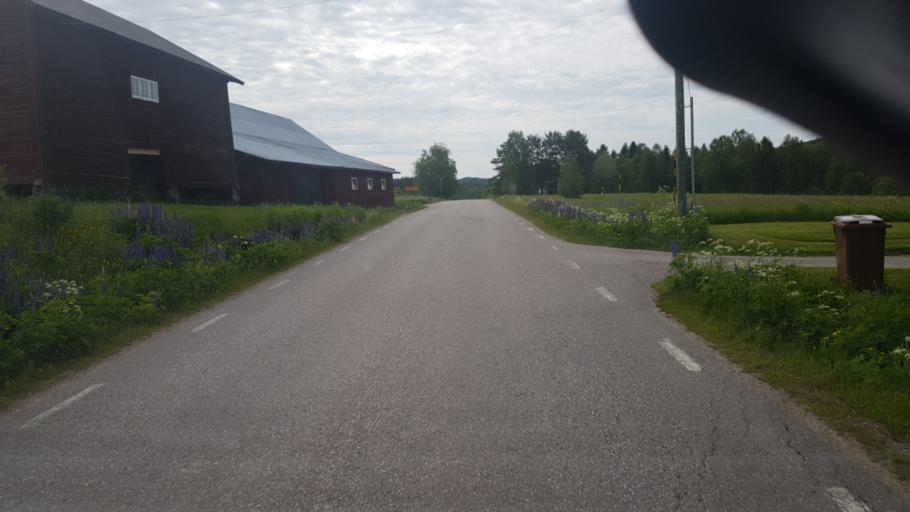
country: SE
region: Vaermland
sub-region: Arvika Kommun
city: Arvika
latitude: 59.7540
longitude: 12.7994
